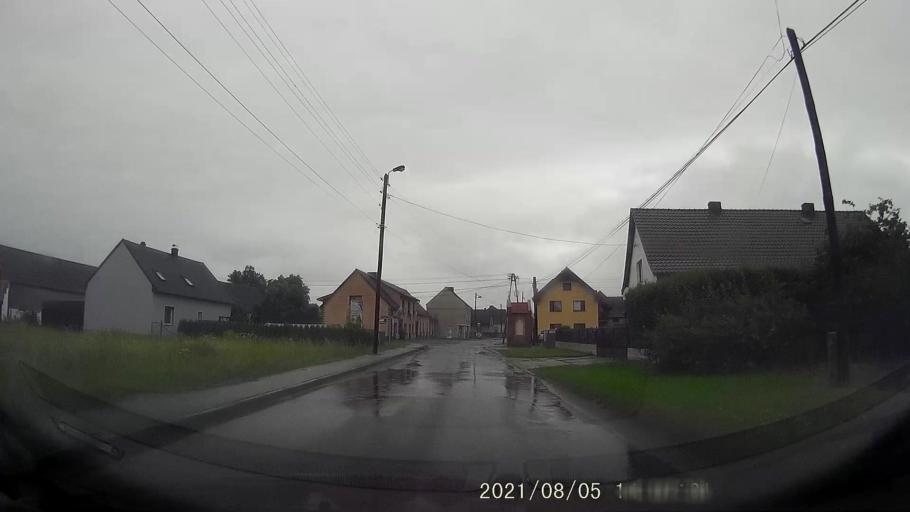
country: PL
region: Opole Voivodeship
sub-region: Powiat krapkowicki
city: Strzeleczki
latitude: 50.4673
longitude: 17.8279
